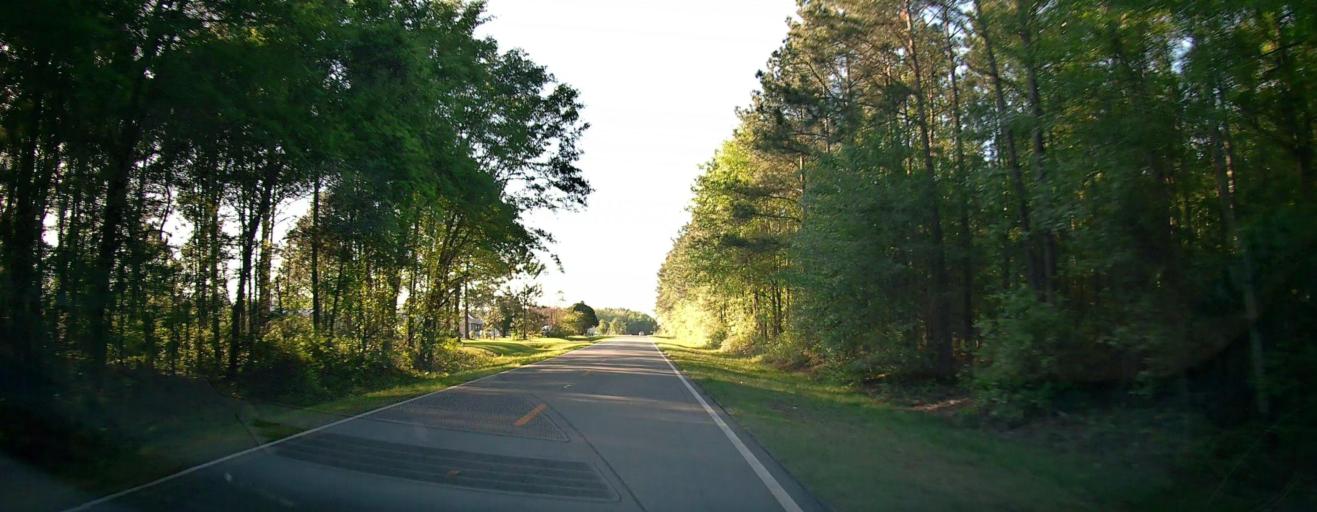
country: US
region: Georgia
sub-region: Ben Hill County
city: Fitzgerald
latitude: 31.6899
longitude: -83.2156
